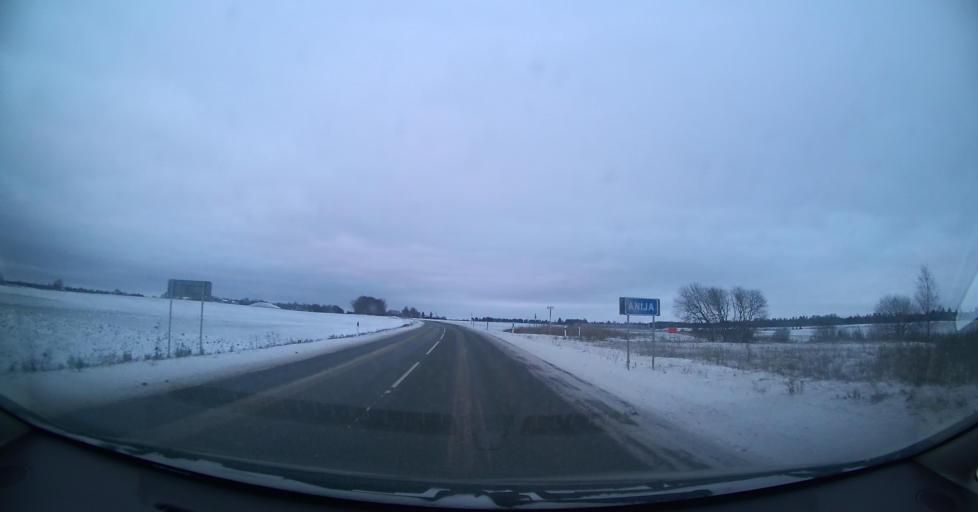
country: EE
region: Harju
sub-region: Anija vald
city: Kehra
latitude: 59.3900
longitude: 25.2873
